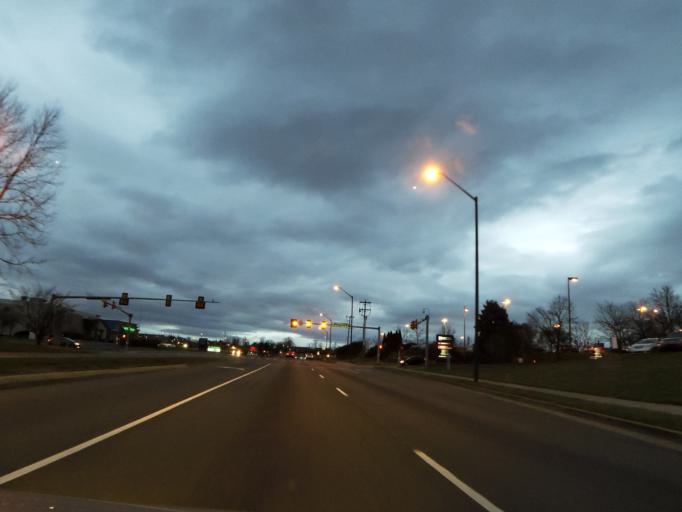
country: US
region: Tennessee
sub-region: Washington County
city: Johnson City
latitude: 36.3078
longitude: -82.3866
